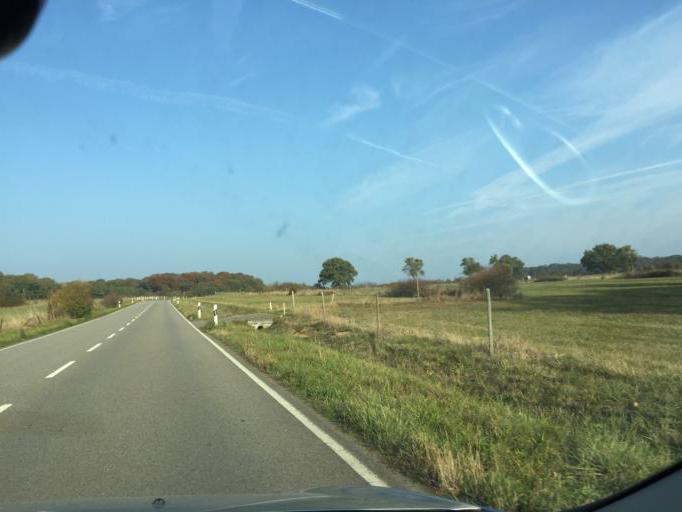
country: LU
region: Luxembourg
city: Aspelt
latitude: 49.5474
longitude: 6.2325
